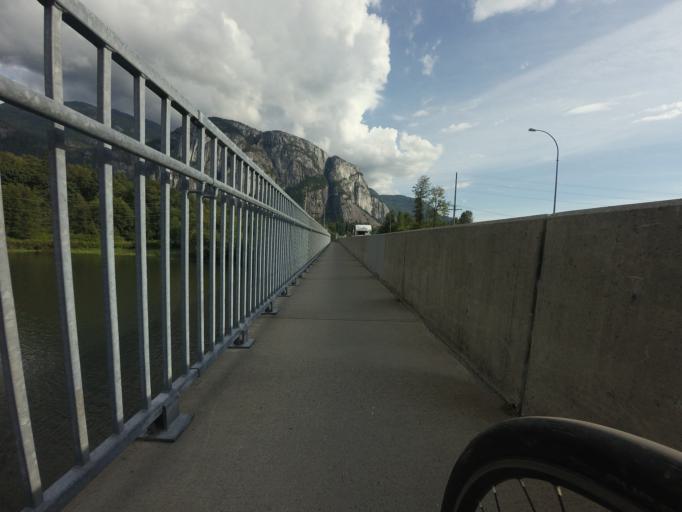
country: CA
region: British Columbia
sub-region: Greater Vancouver Regional District
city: Lions Bay
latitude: 49.7017
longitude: -123.1445
